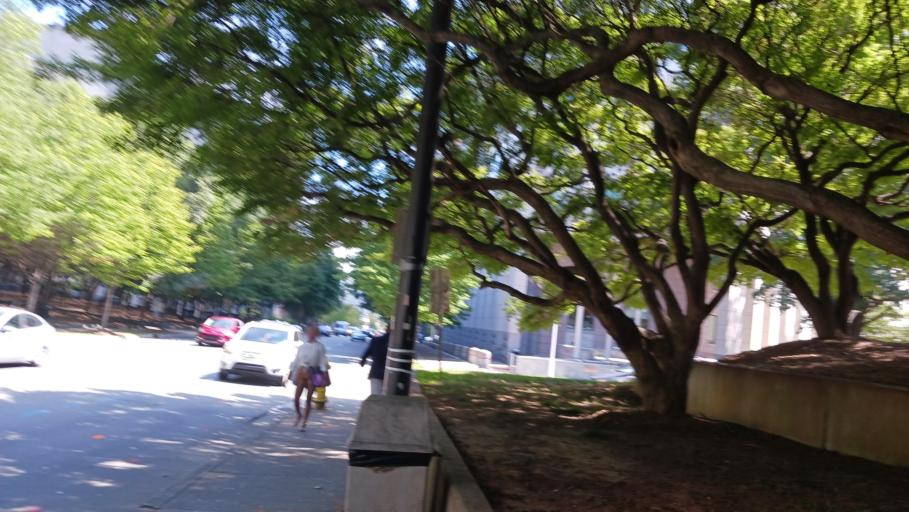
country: US
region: North Carolina
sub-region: Mecklenburg County
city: Charlotte
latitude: 35.2207
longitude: -80.8378
